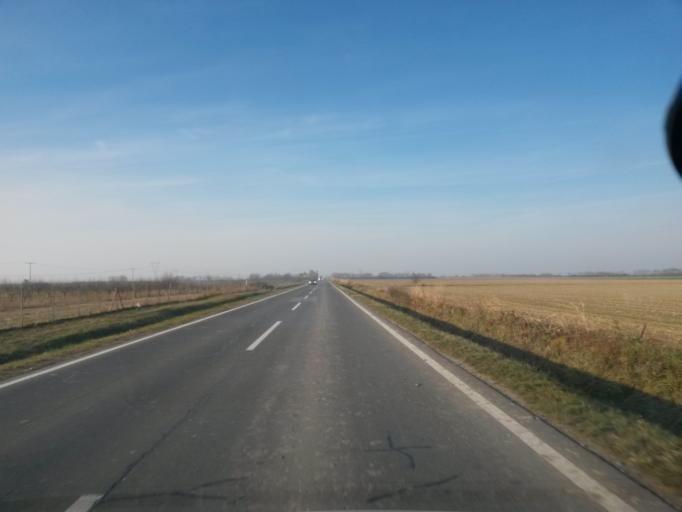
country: HR
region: Osjecko-Baranjska
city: Laslovo
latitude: 45.4272
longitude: 18.6810
